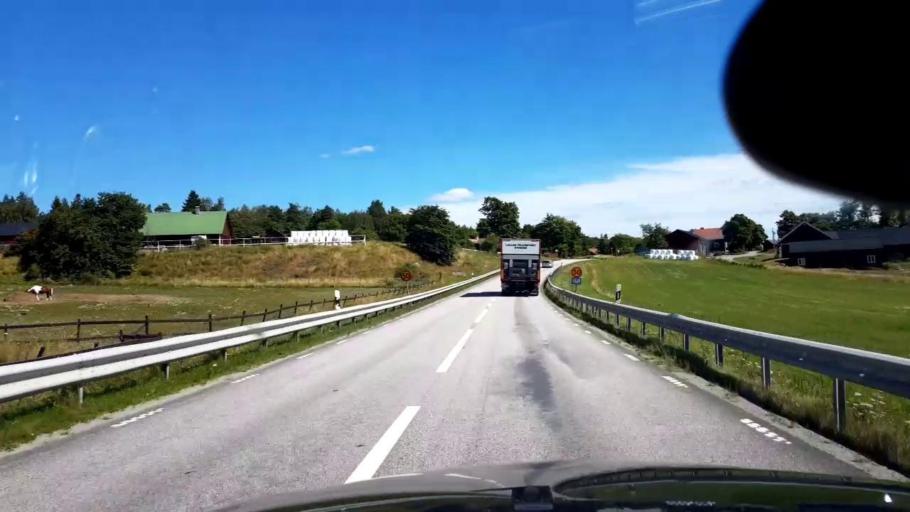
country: SE
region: Stockholm
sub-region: Sigtuna Kommun
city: Sigtuna
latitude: 59.6576
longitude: 17.6746
